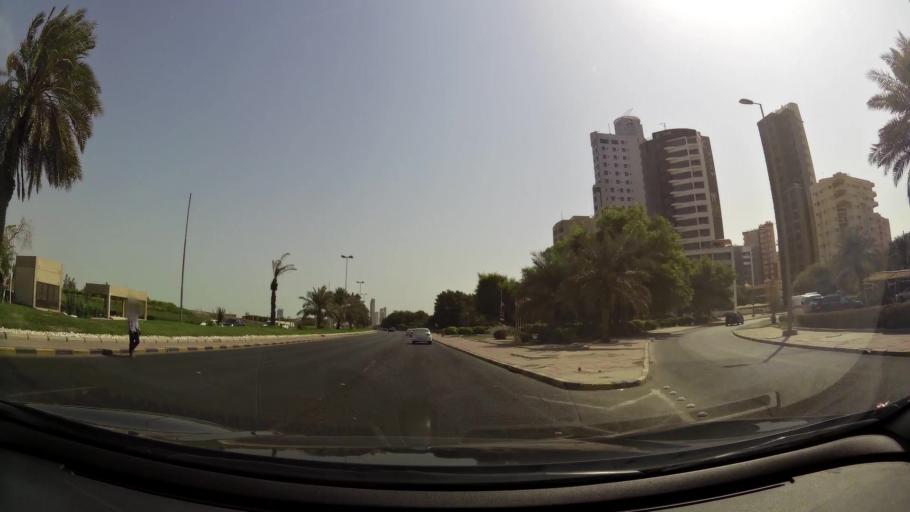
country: KW
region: Muhafazat Hawalli
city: Hawalli
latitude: 29.3515
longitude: 48.0312
